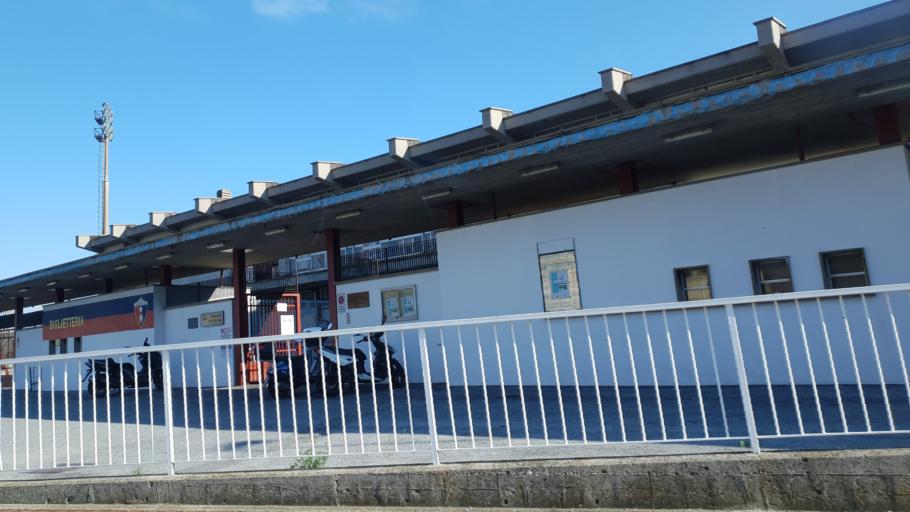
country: IT
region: Liguria
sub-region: Provincia di Savona
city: Valleggia
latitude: 44.2777
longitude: 8.4343
